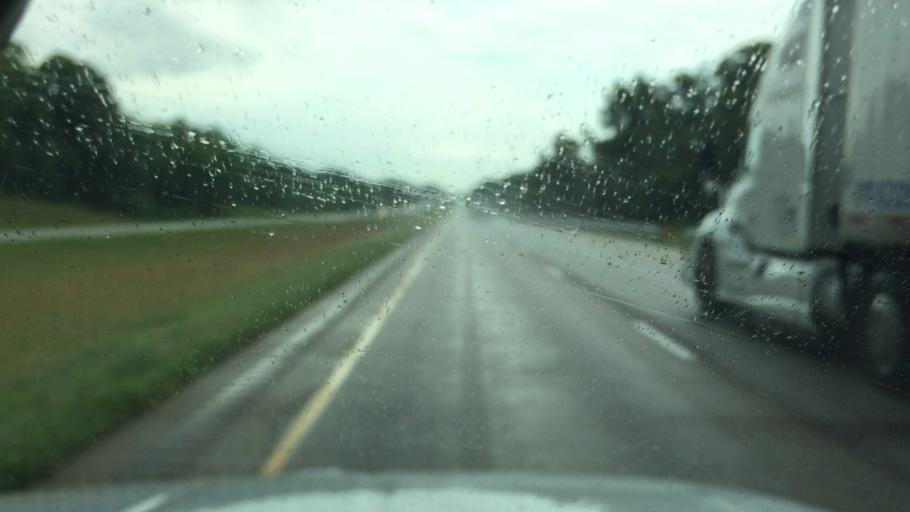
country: US
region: Illinois
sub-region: Peoria County
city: Bellevue
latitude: 40.7510
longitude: -89.6953
